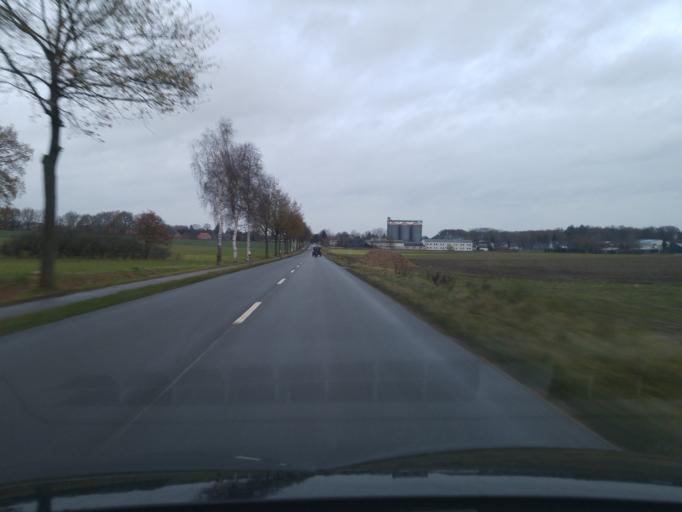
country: DE
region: Lower Saxony
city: Scharnebeck
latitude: 53.2799
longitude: 10.5031
